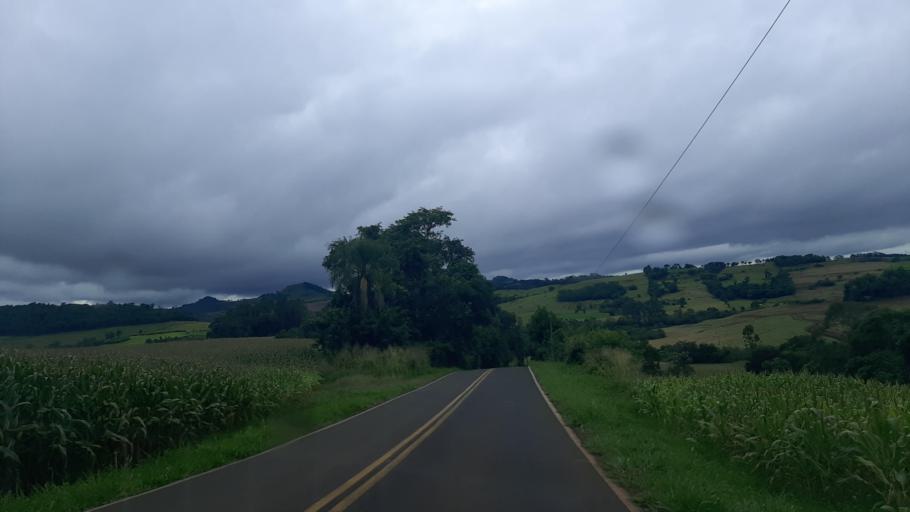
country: BR
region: Parana
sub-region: Ampere
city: Ampere
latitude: -25.9926
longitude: -53.4385
